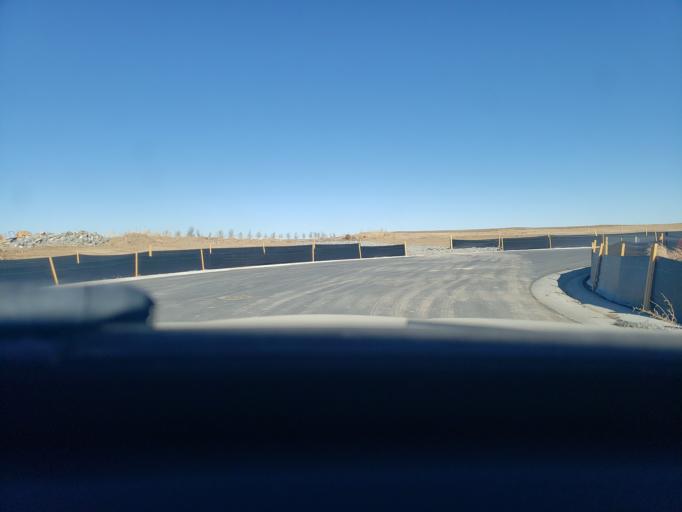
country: US
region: Colorado
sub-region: Adams County
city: Aurora
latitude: 39.7746
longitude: -104.7054
